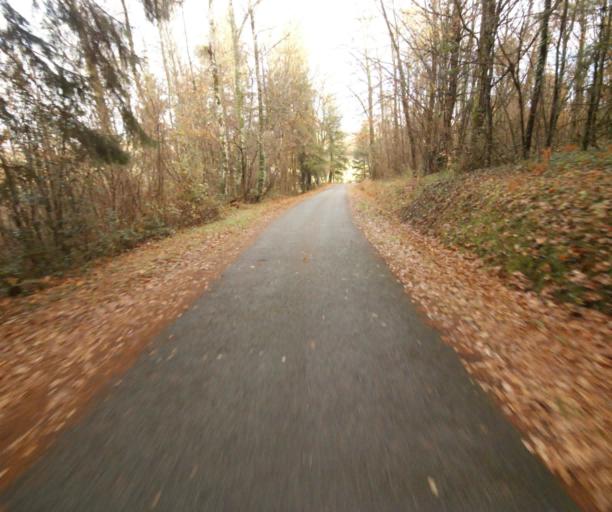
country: FR
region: Limousin
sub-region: Departement de la Correze
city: Saint-Mexant
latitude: 45.2619
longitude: 1.6280
